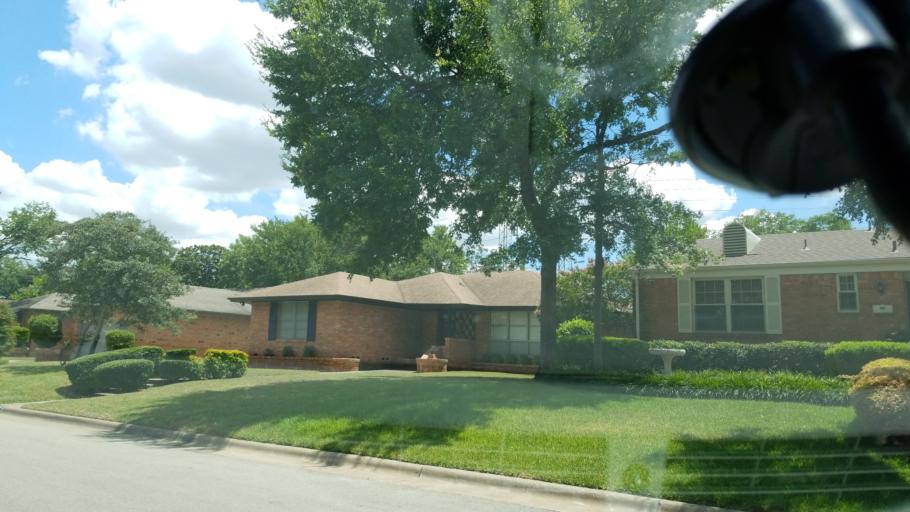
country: US
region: Texas
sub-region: Dallas County
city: Cockrell Hill
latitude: 32.7014
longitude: -96.8772
